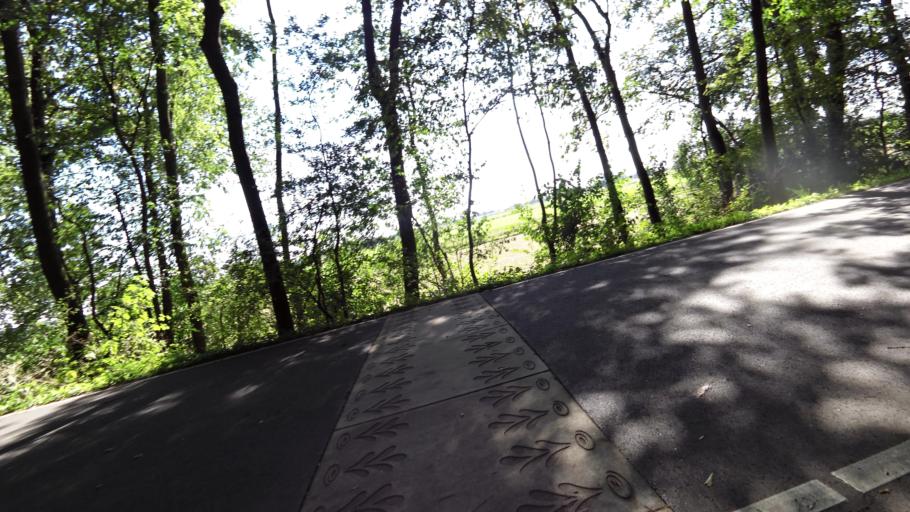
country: NL
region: Gelderland
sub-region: Gemeente Renkum
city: Doorwerth
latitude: 51.9689
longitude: 5.7964
